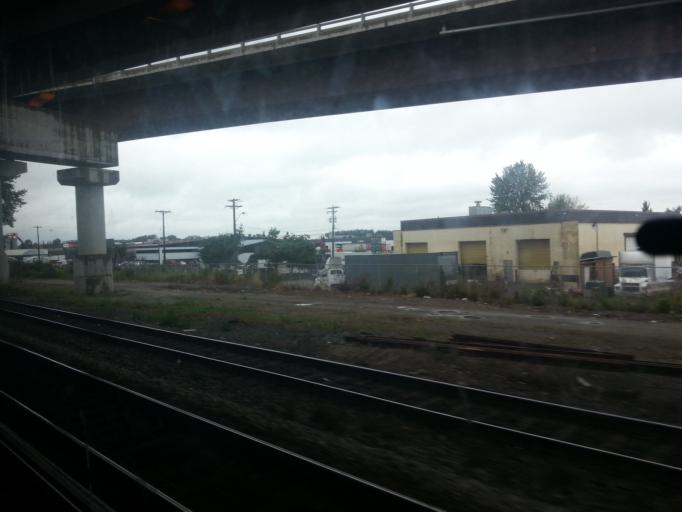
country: CA
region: British Columbia
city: Walnut Grove
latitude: 49.1831
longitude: -122.6673
